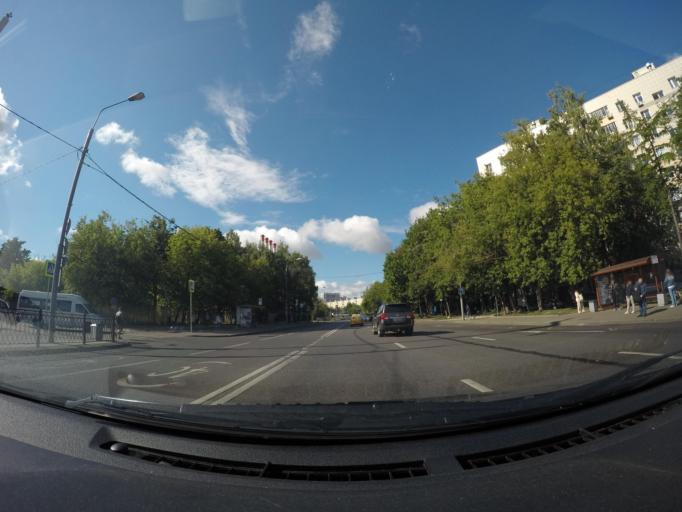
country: RU
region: Moscow
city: Khimki
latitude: 55.8610
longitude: 37.4341
